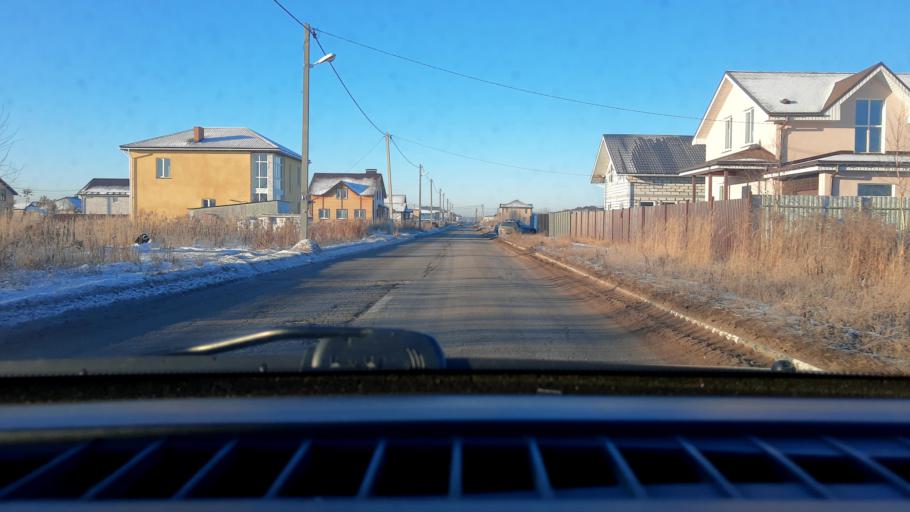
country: RU
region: Nizjnij Novgorod
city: Bor
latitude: 56.3899
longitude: 44.0696
